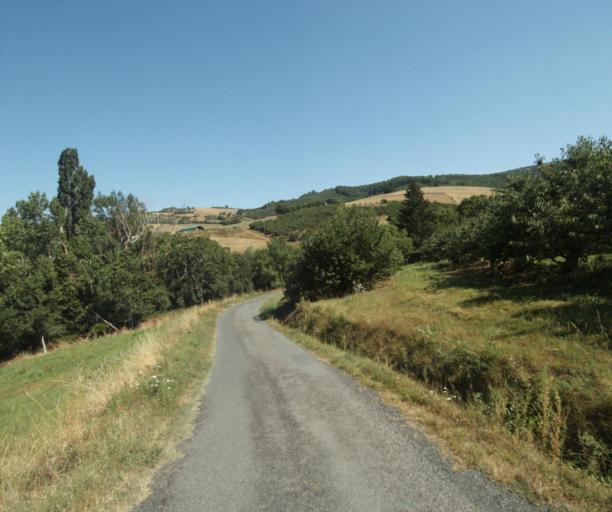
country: FR
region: Rhone-Alpes
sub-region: Departement du Rhone
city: Courzieu
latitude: 45.7442
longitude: 4.5407
